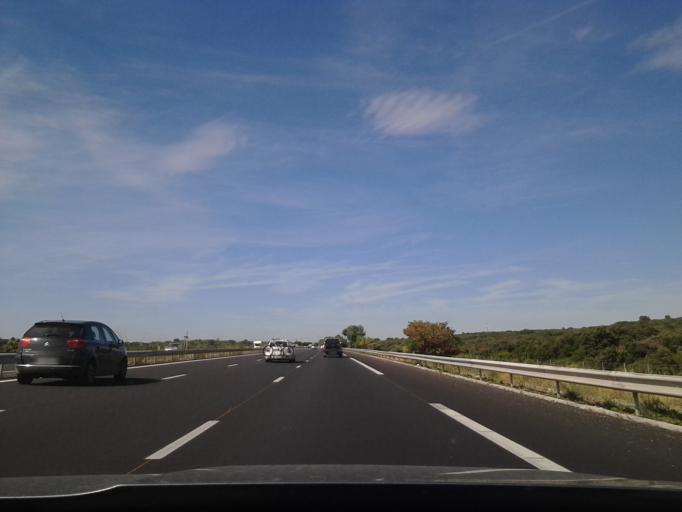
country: FR
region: Languedoc-Roussillon
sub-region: Departement de l'Herault
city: Bouzigues
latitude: 43.4718
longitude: 3.6436
